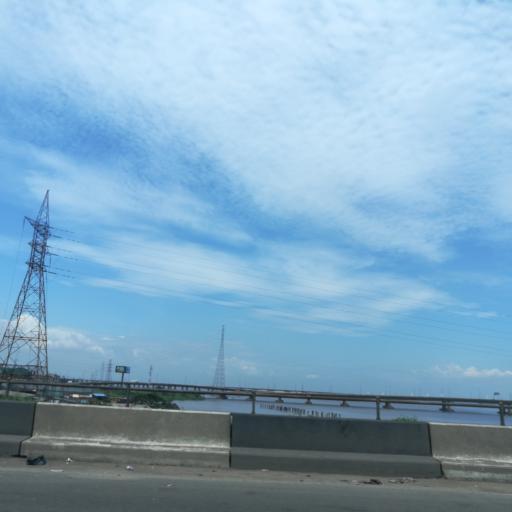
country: NG
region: Lagos
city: Lagos
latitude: 6.4658
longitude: 3.3798
